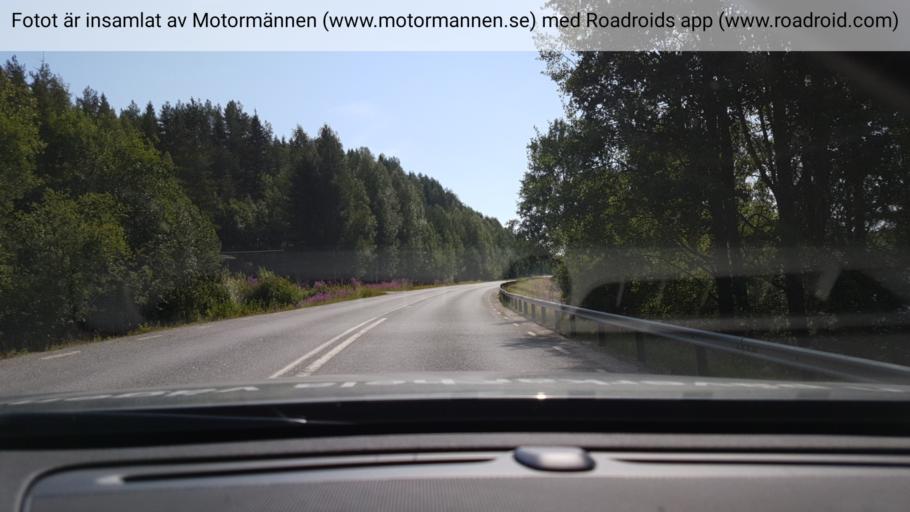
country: SE
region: Vaesterbotten
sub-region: Vindelns Kommun
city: Vindeln
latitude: 64.3112
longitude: 19.6069
